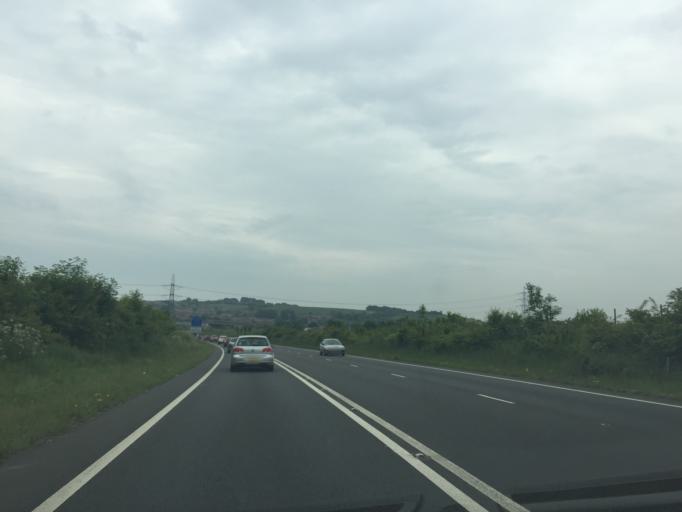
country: GB
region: England
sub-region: Dorset
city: Overcombe
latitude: 50.6563
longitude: -2.4629
